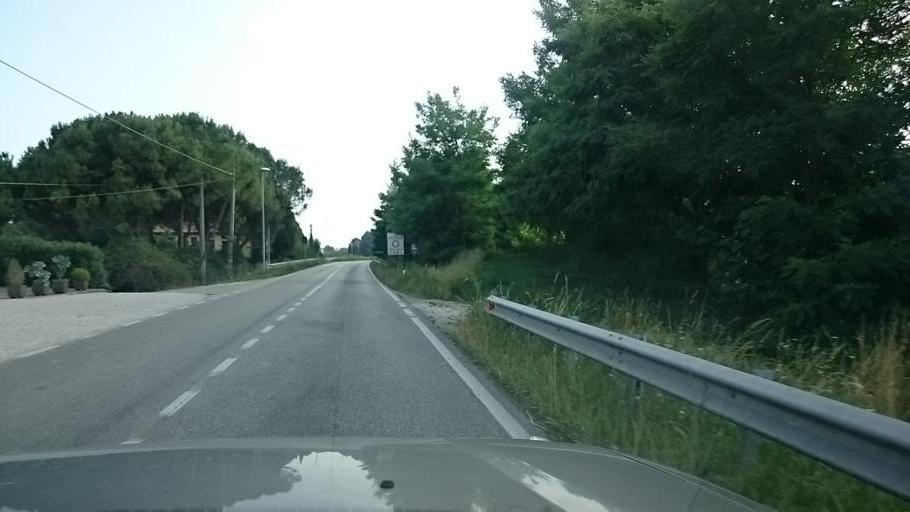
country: IT
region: Veneto
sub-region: Provincia di Padova
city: Santa Maria di Non
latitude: 45.5141
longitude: 11.8648
